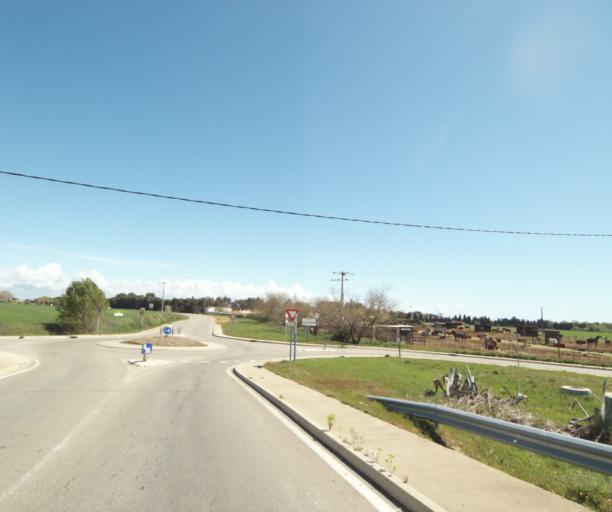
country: FR
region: Languedoc-Roussillon
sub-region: Departement de l'Herault
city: Villeneuve-les-Maguelone
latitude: 43.5561
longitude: 3.8602
